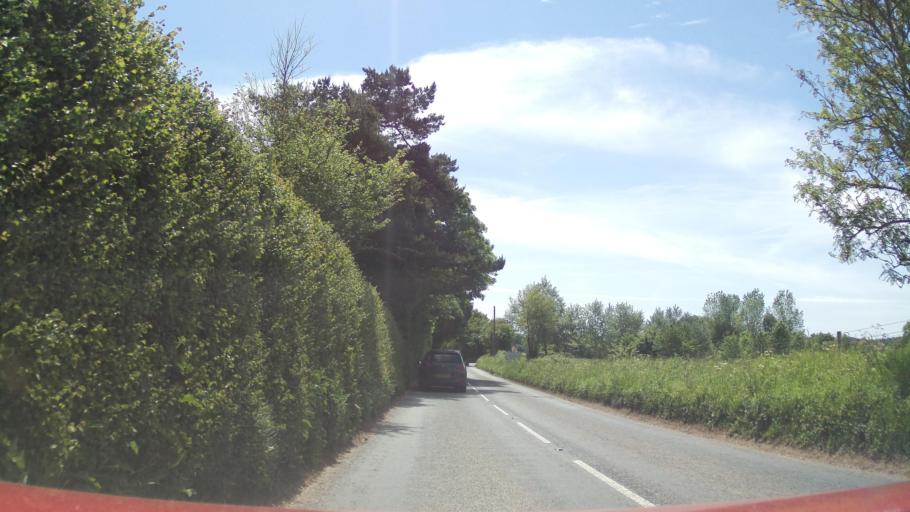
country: GB
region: England
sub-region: Devon
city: Uffculme
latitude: 50.8320
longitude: -3.3010
